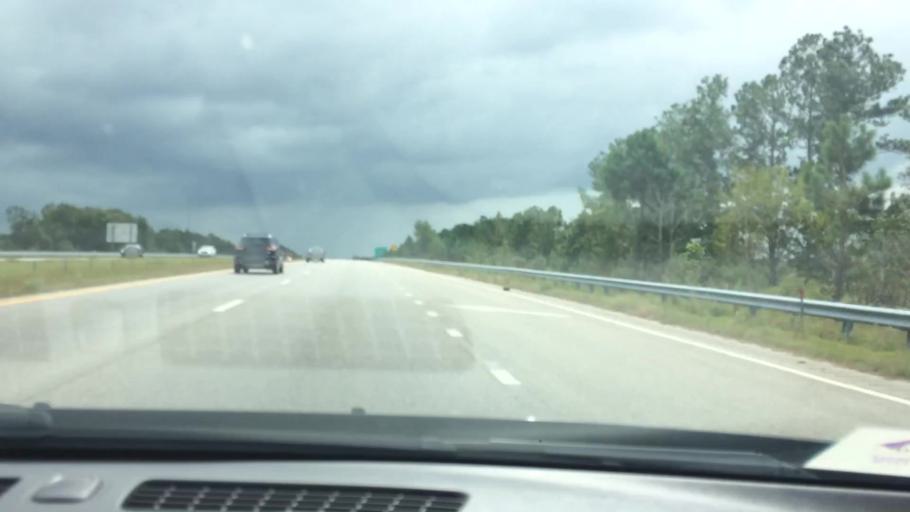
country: US
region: North Carolina
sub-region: Wilson County
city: Lucama
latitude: 35.7549
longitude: -78.0254
